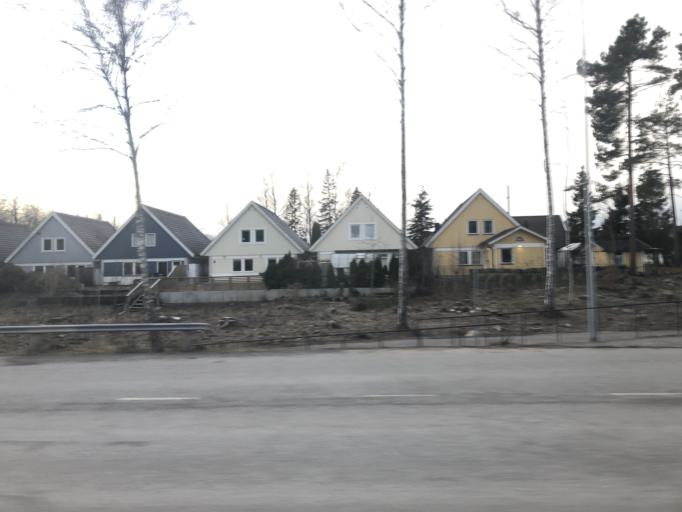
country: SE
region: Stockholm
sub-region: Jarfalla Kommun
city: Jakobsberg
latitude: 59.4054
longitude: 17.7958
